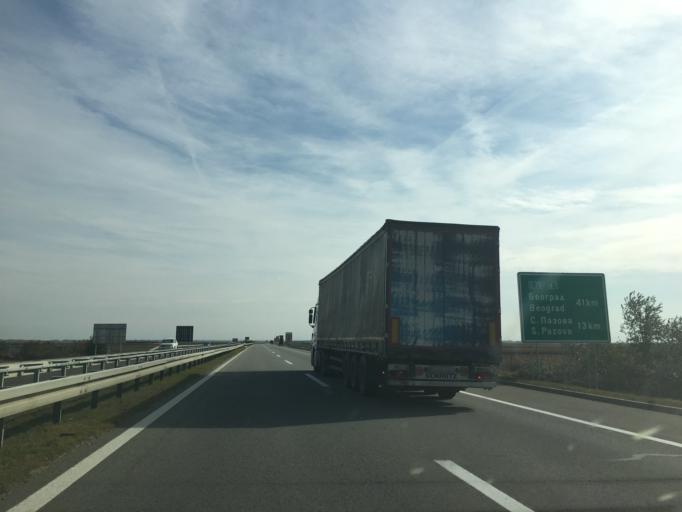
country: RS
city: Novi Karlovci
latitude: 45.0660
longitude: 20.1566
